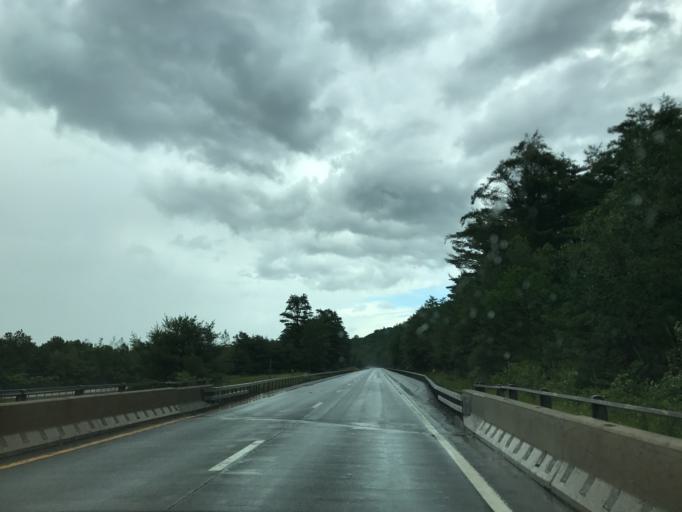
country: US
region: New York
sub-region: Warren County
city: Warrensburg
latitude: 43.4995
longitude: -73.7470
